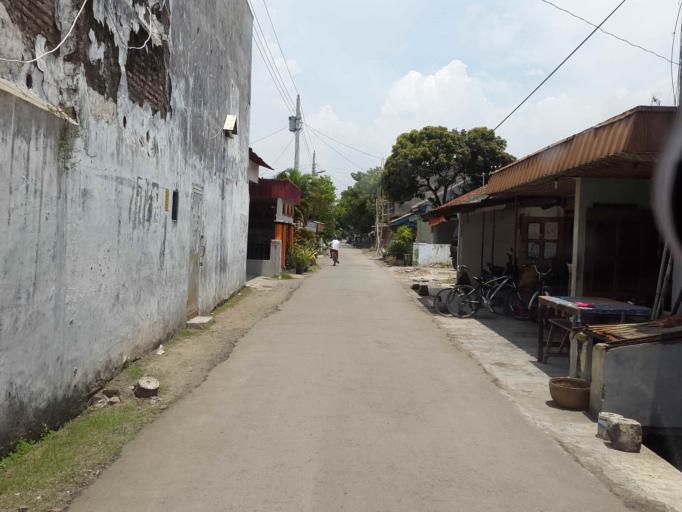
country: ID
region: Central Java
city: Pemalang
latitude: -6.8907
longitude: 109.3903
